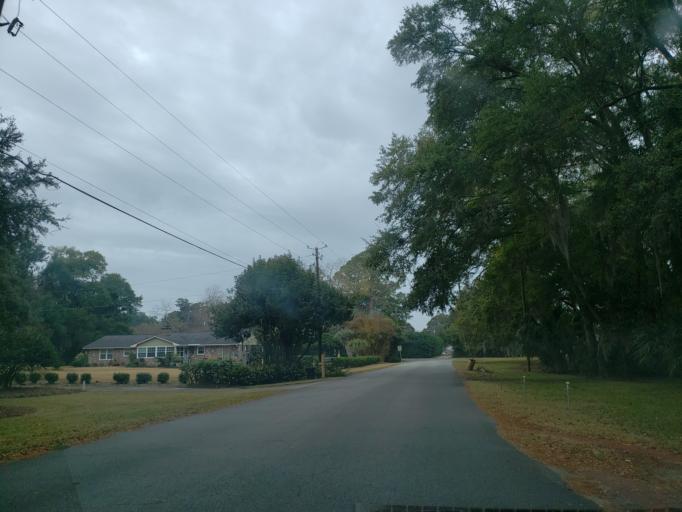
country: US
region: Georgia
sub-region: Chatham County
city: Wilmington Island
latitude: 31.9814
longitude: -80.9959
